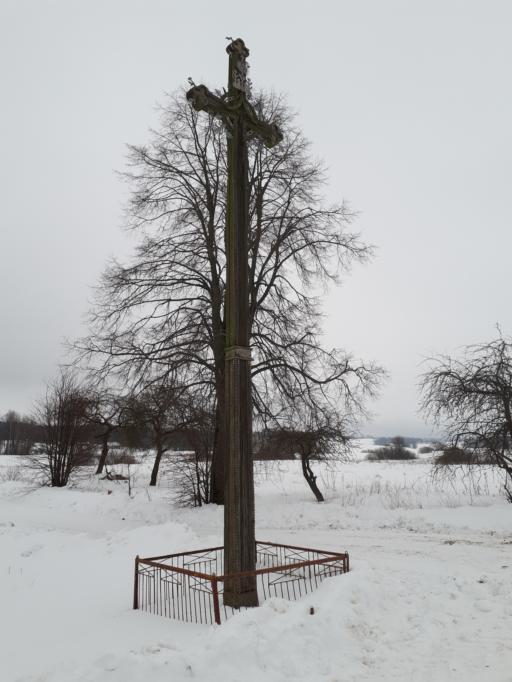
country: LT
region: Alytaus apskritis
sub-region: Alytus
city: Alytus
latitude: 54.4597
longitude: 24.1694
